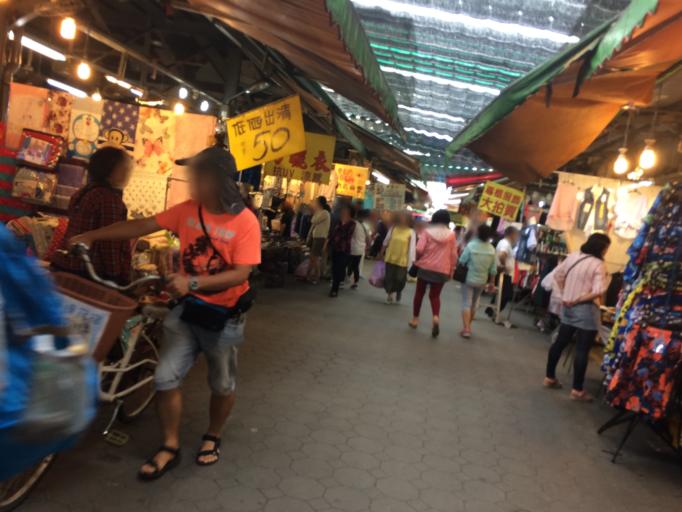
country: TW
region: Taiwan
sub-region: Hualien
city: Hualian
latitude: 23.9773
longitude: 121.6102
